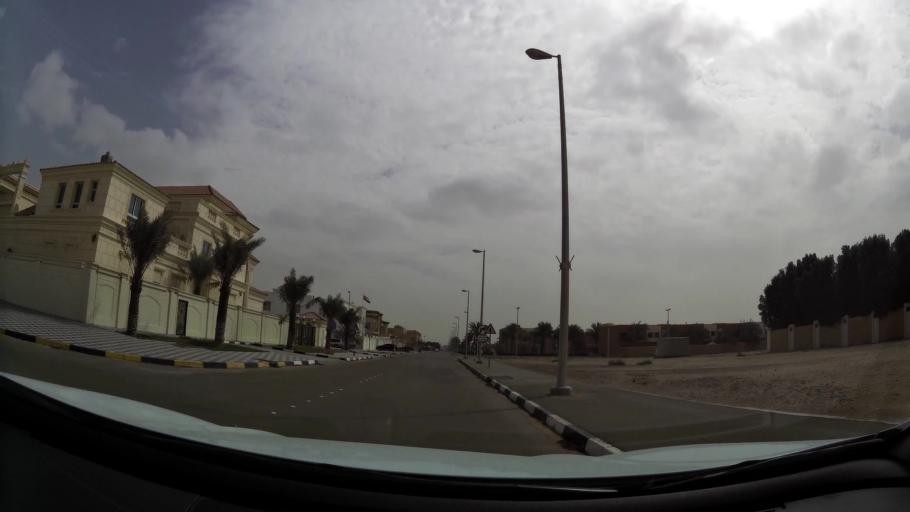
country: AE
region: Abu Dhabi
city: Abu Dhabi
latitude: 24.3947
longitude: 54.4905
